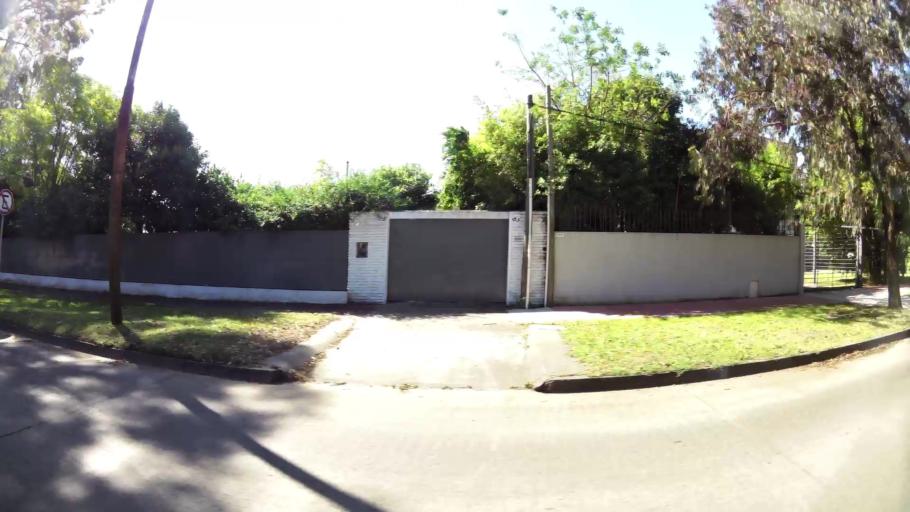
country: UY
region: Canelones
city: Paso de Carrasco
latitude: -34.8881
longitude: -56.0640
